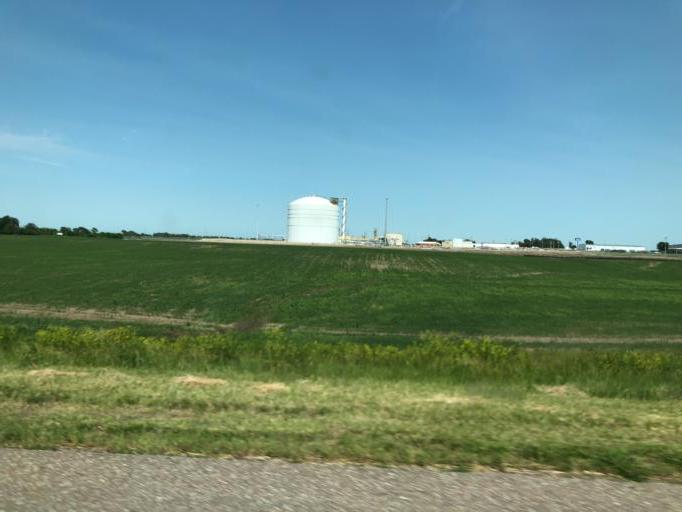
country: US
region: Nebraska
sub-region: Fillmore County
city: Geneva
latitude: 40.5400
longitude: -97.5868
